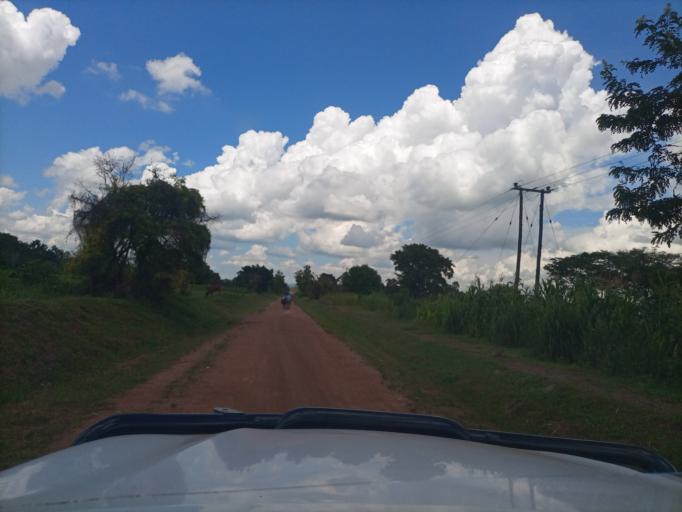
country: UG
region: Eastern Region
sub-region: Tororo District
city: Tororo
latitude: 0.6774
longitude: 34.0062
